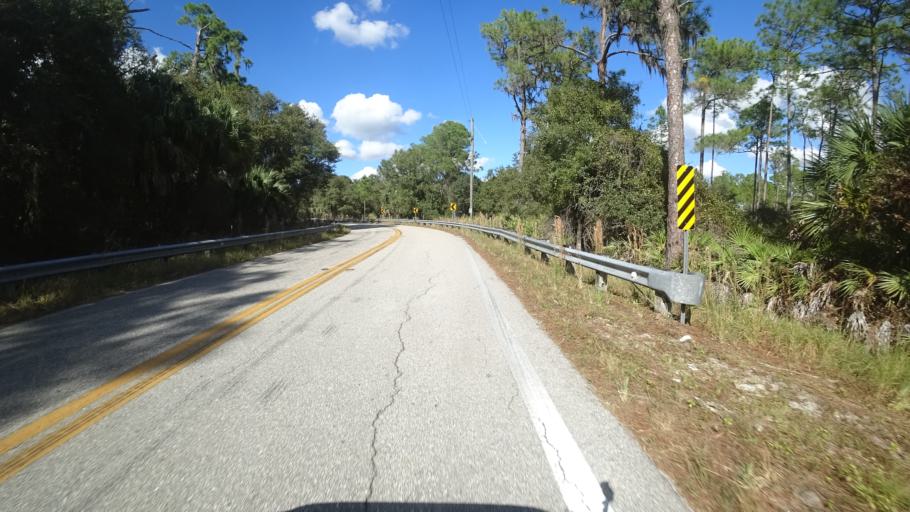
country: US
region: Florida
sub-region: Sarasota County
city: North Port
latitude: 27.2169
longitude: -82.1217
